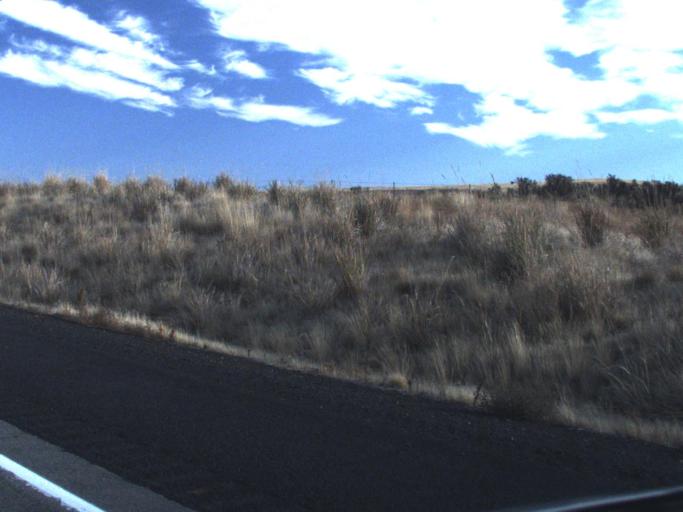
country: US
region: Washington
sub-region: Adams County
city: Ritzville
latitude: 46.8965
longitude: -118.6125
